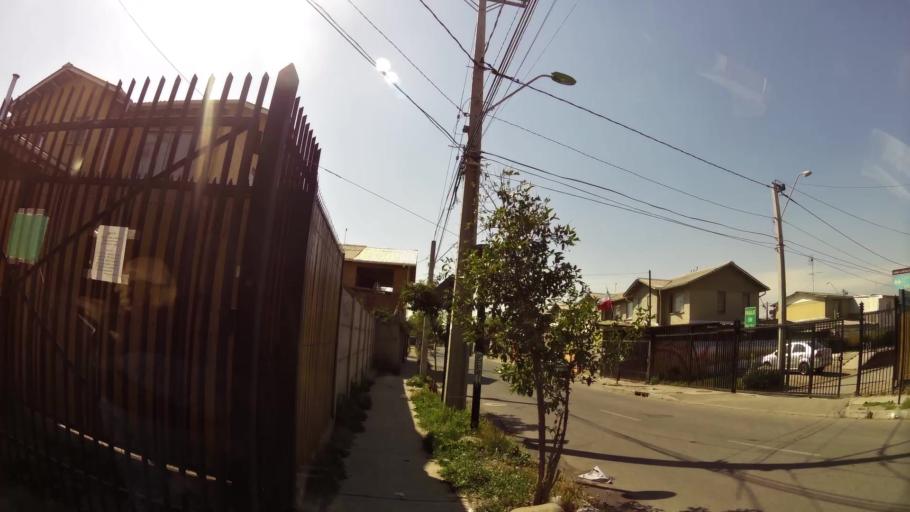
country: CL
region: Santiago Metropolitan
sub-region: Provincia de Santiago
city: La Pintana
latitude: -33.5643
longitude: -70.6272
